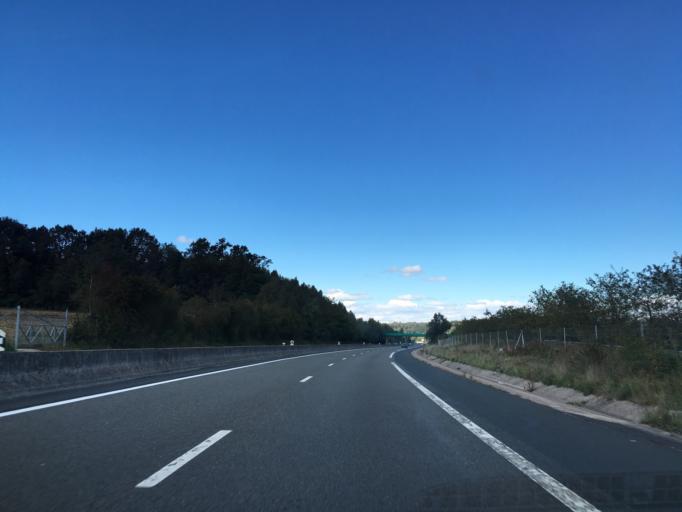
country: FR
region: Lorraine
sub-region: Departement de Meurthe-et-Moselle
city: Baccarat
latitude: 48.4144
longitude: 6.7973
